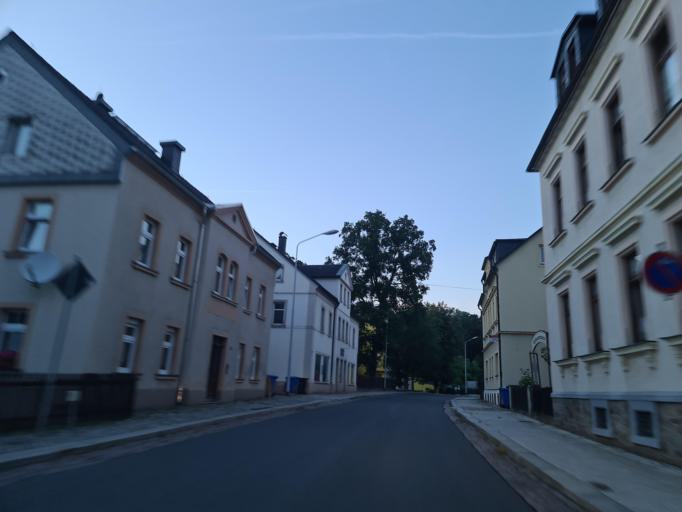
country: DE
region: Saxony
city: Neuhausen
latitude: 50.6766
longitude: 13.4665
